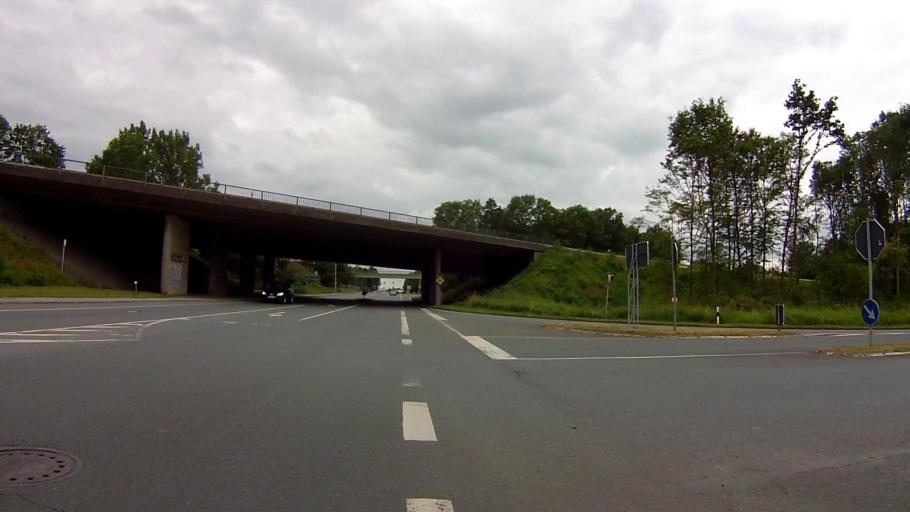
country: DE
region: North Rhine-Westphalia
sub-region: Regierungsbezirk Detmold
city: Paderborn
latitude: 51.7020
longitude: 8.7421
